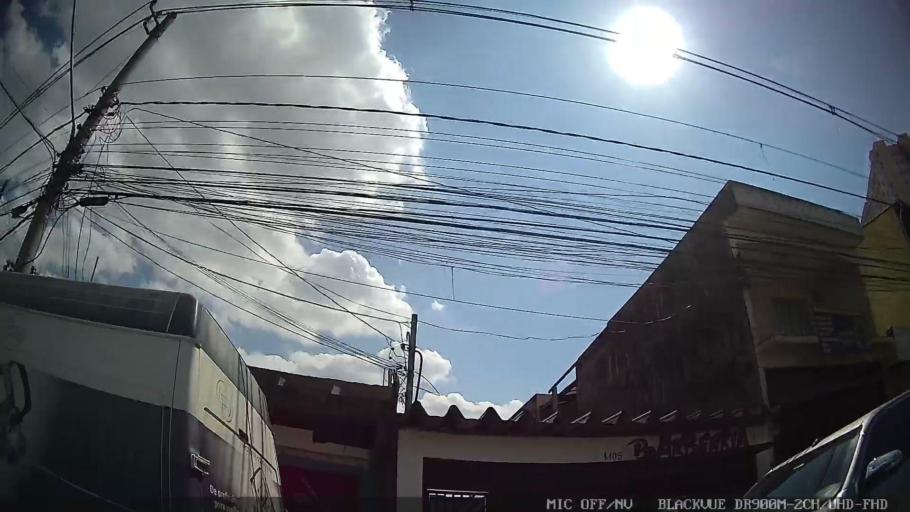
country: BR
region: Sao Paulo
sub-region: Guarulhos
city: Guarulhos
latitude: -23.4875
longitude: -46.4695
